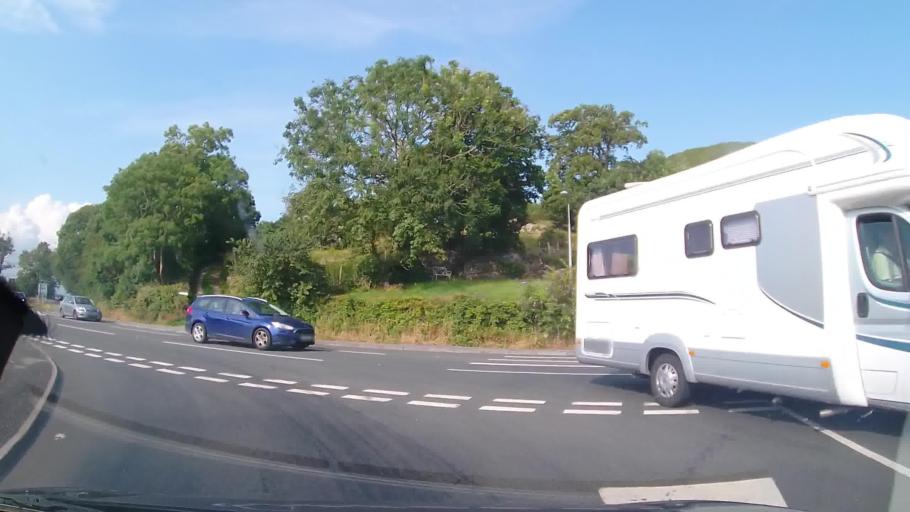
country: GB
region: Wales
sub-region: Gwynedd
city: Penrhyndeudraeth
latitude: 52.8937
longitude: -4.0722
